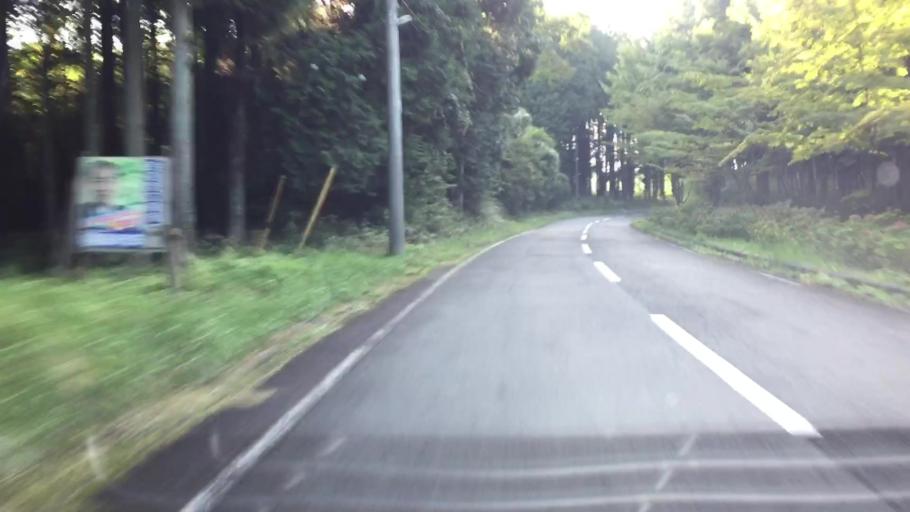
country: JP
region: Tochigi
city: Imaichi
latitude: 36.7629
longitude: 139.6931
